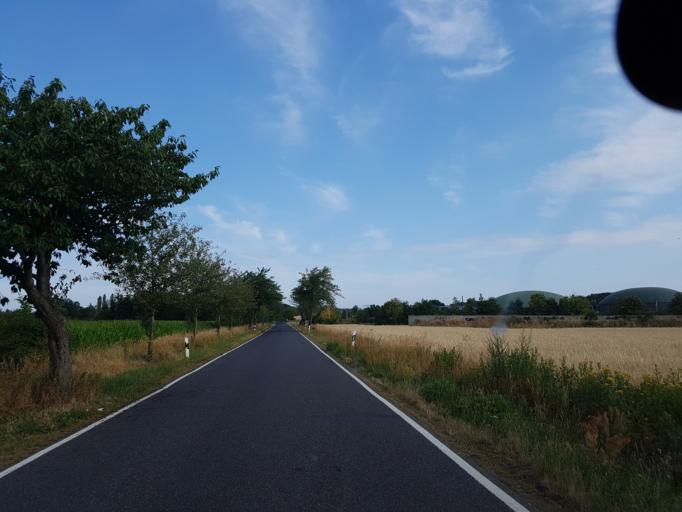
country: DE
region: Brandenburg
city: Drahnsdorf
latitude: 51.8486
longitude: 13.6232
